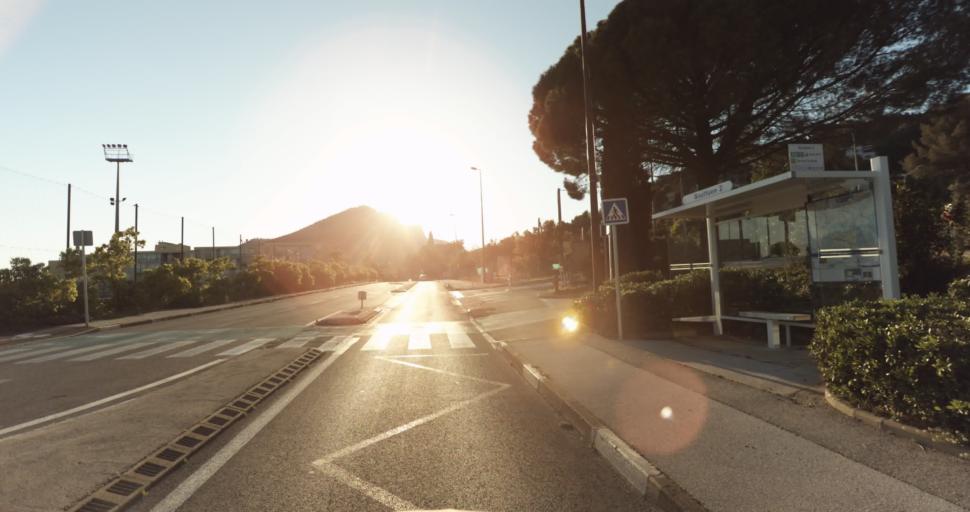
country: FR
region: Provence-Alpes-Cote d'Azur
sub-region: Departement du Var
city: La Valette-du-Var
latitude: 43.1425
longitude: 5.9956
